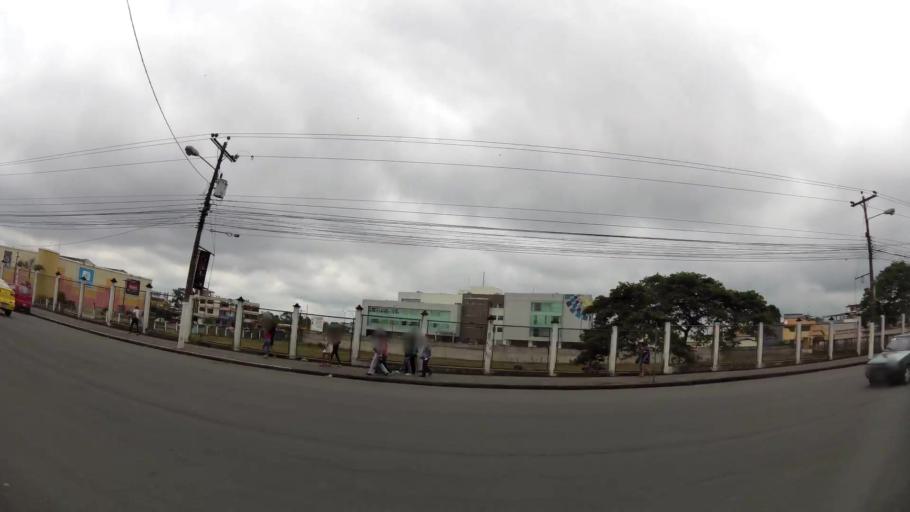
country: EC
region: Santo Domingo de los Tsachilas
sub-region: Canton Santo Domingo de los Colorados
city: Santo Domingo de los Colorados
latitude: -0.2491
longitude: -79.1601
